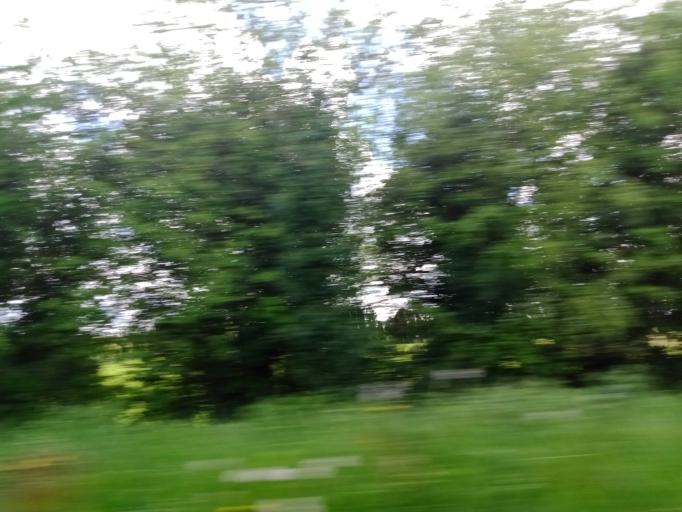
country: IE
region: Munster
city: Thurles
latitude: 52.6762
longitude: -7.6720
